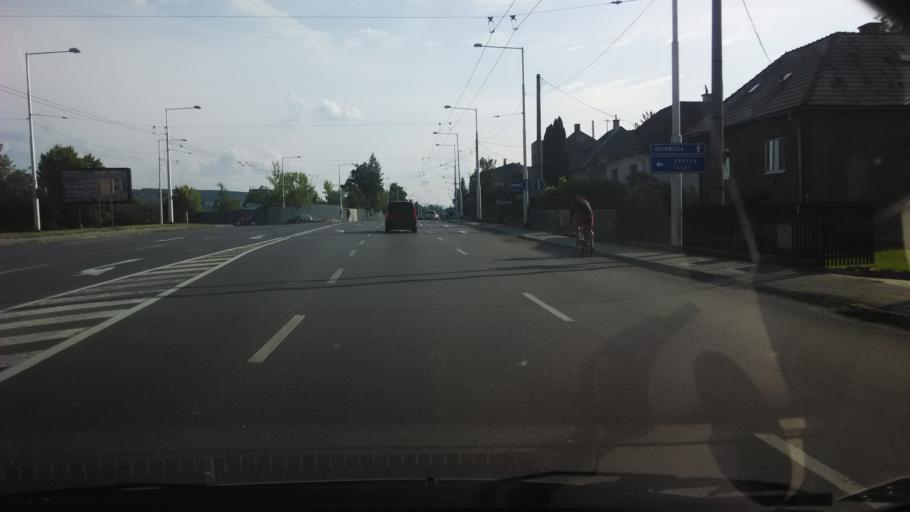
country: SK
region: Banskobystricky
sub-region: Okres Banska Bystrica
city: Banska Bystrica
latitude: 48.7180
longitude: 19.1323
